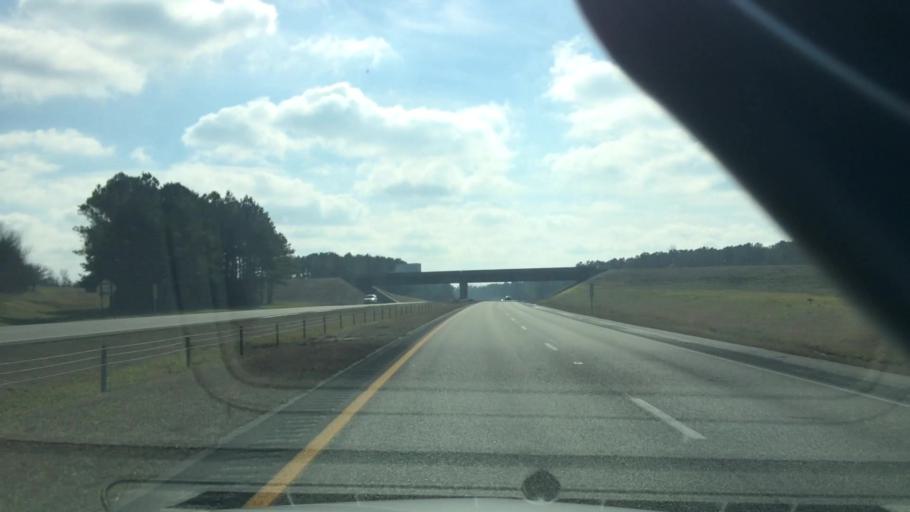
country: US
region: North Carolina
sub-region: Duplin County
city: Wallace
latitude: 34.6893
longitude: -77.9460
